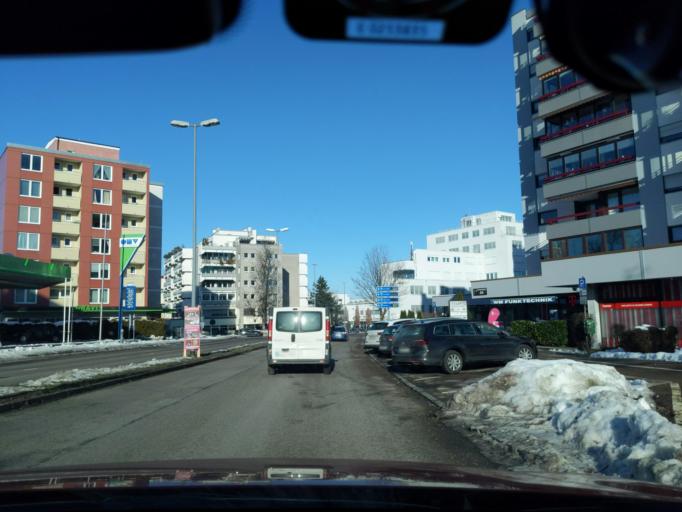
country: DE
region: Bavaria
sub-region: Swabia
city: Kempten (Allgaeu)
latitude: 47.7178
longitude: 10.3143
